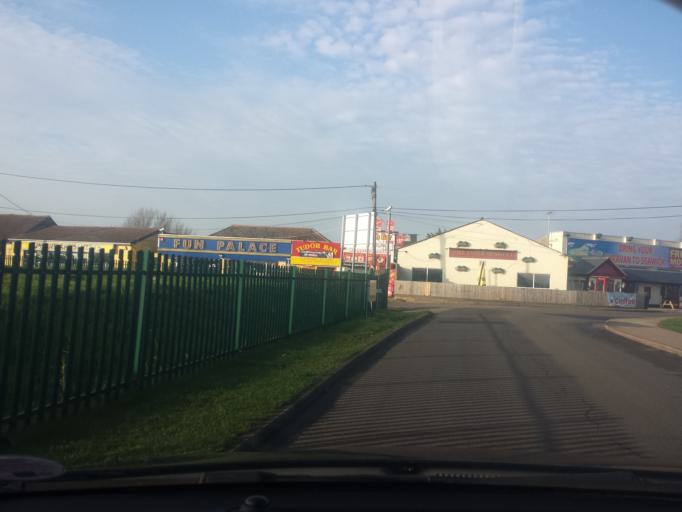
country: GB
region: England
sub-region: Essex
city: Saint Osyth
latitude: 51.7762
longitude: 1.0867
